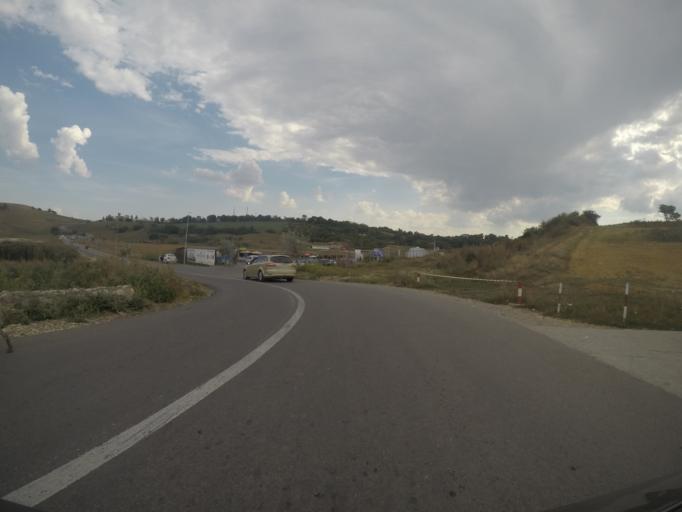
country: RO
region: Cluj
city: Turda
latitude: 46.5894
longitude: 23.7873
